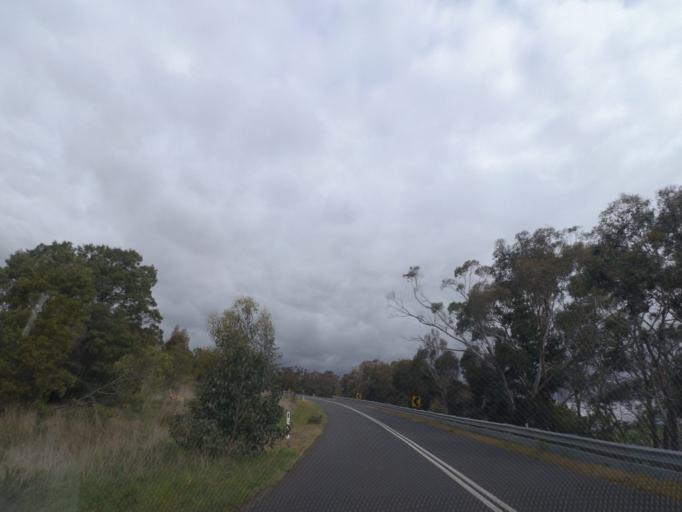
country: AU
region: Victoria
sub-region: Hume
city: Sunbury
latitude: -37.3552
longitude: 144.8029
